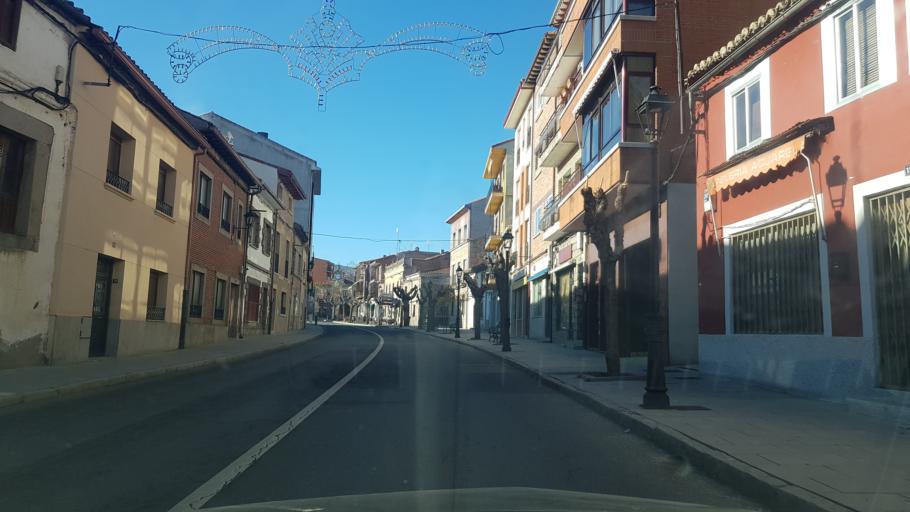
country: ES
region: Castille and Leon
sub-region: Provincia de Avila
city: Barraco
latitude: 40.4766
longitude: -4.6415
